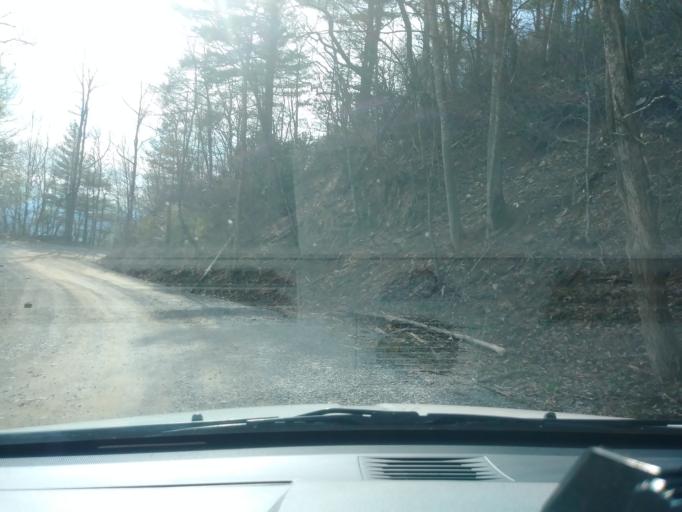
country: US
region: Tennessee
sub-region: Greene County
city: Tusculum
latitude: 36.0329
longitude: -82.7248
